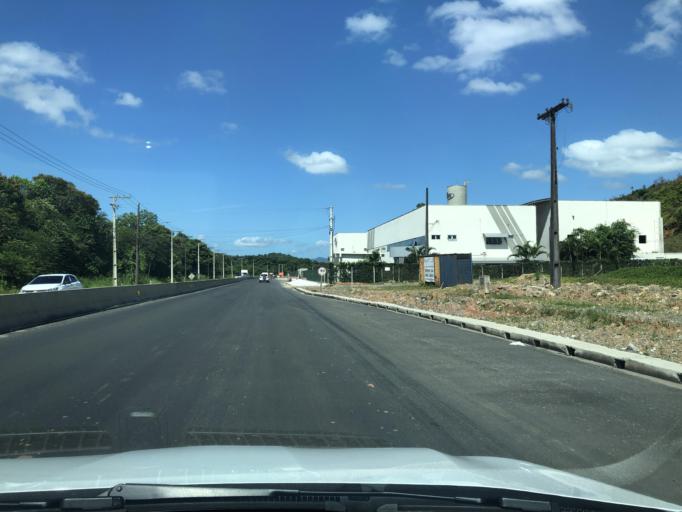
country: BR
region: Santa Catarina
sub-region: Joinville
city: Joinville
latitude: -26.2520
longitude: -48.8679
